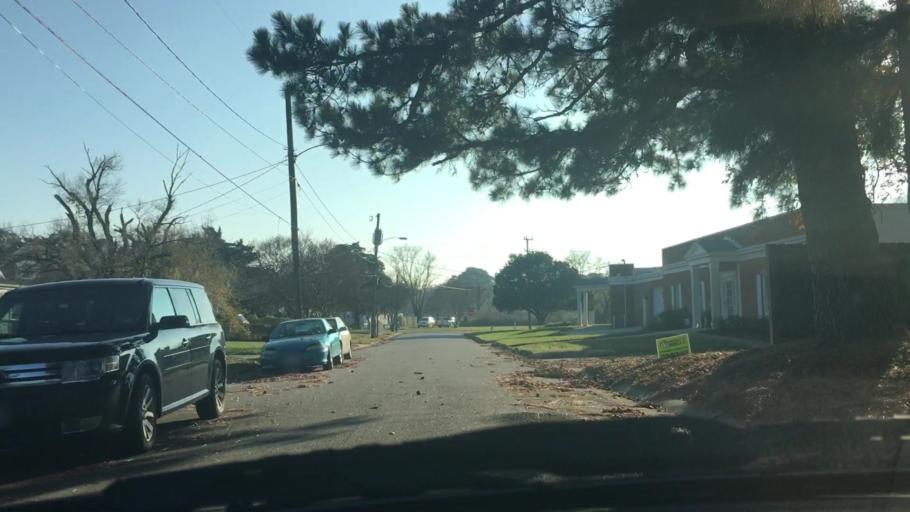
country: US
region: Virginia
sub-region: City of Norfolk
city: Norfolk
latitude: 36.8922
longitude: -76.2559
